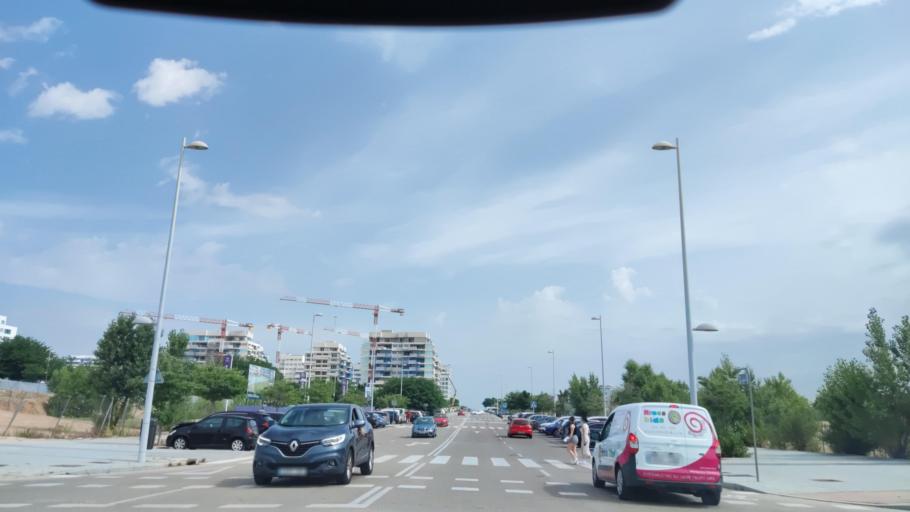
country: ES
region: Madrid
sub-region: Provincia de Madrid
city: Barajas de Madrid
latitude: 40.4876
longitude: -3.6065
